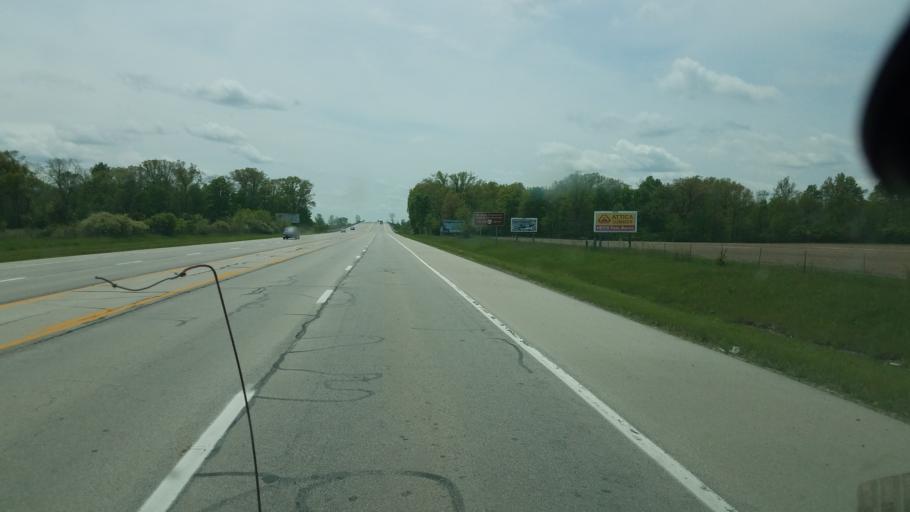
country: US
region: Ohio
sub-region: Sandusky County
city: Fremont
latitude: 41.3908
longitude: -83.1121
